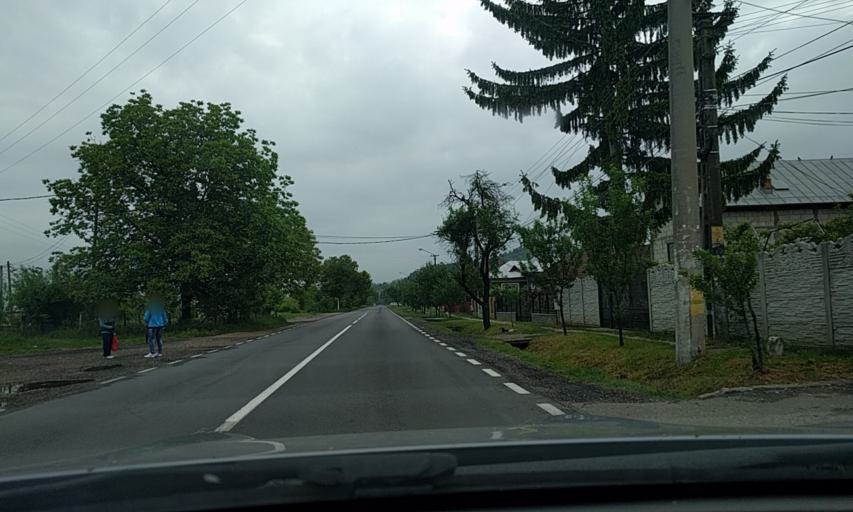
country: RO
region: Dambovita
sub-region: Comuna Branesti
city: Branesti
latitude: 45.0230
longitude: 25.4167
